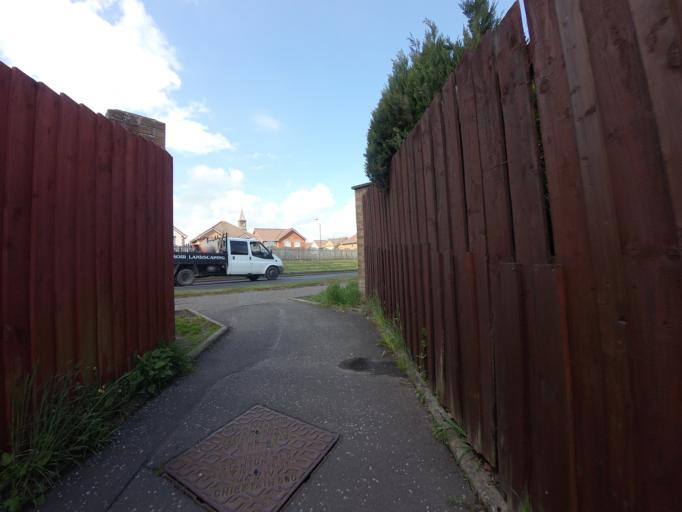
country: GB
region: Scotland
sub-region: Falkirk
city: Falkirk
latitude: 56.0222
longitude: -3.7932
